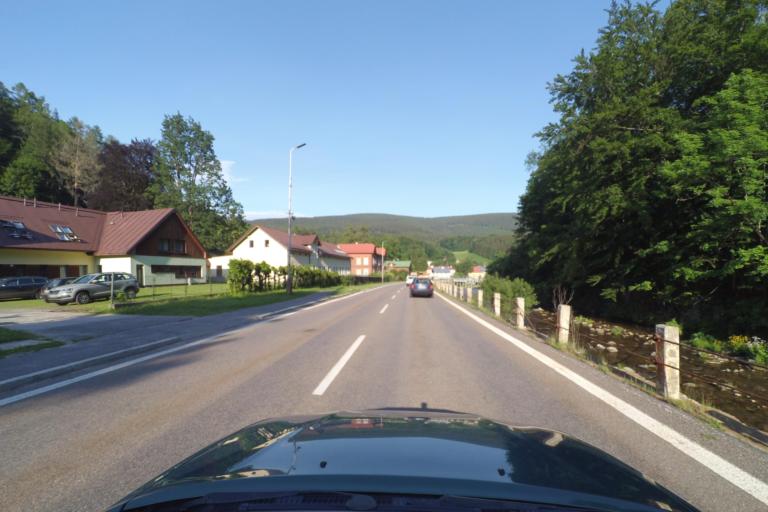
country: CZ
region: Kralovehradecky
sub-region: Okres Trutnov
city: Svoboda nad Upou
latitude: 50.6621
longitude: 15.8147
